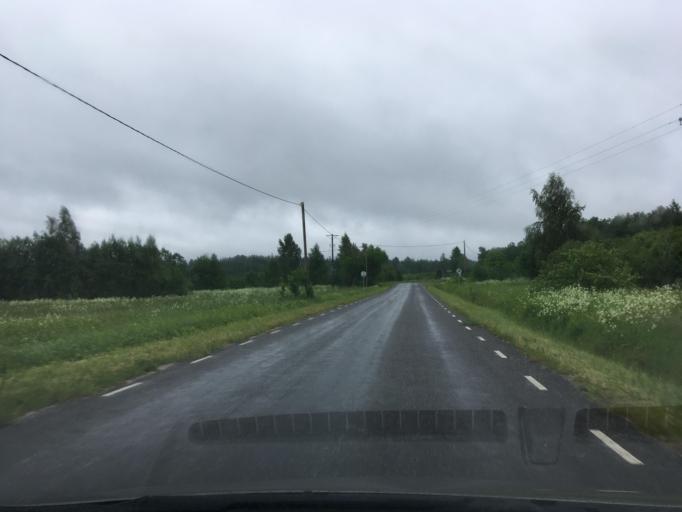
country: EE
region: Laeaene
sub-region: Lihula vald
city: Lihula
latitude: 58.6561
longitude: 23.7741
